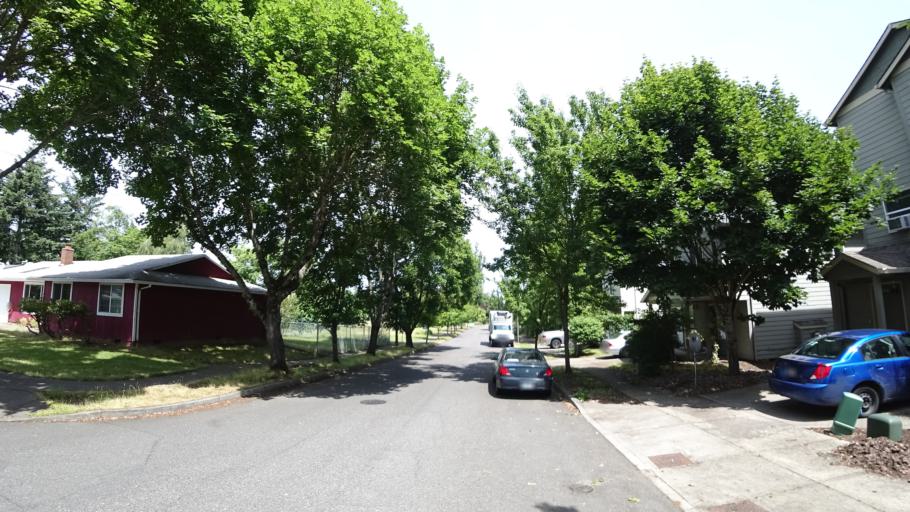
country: US
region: Oregon
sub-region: Multnomah County
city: Fairview
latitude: 45.5491
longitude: -122.5040
